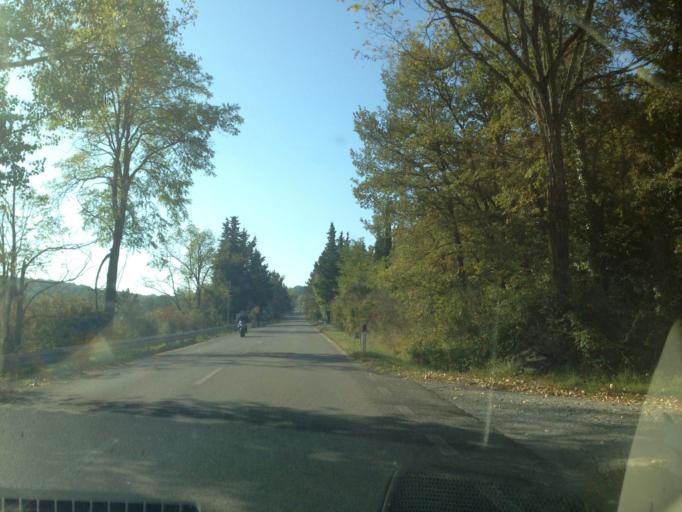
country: IT
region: Tuscany
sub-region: Provincia di Siena
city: Castellina in Chianti
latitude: 43.4890
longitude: 11.2997
